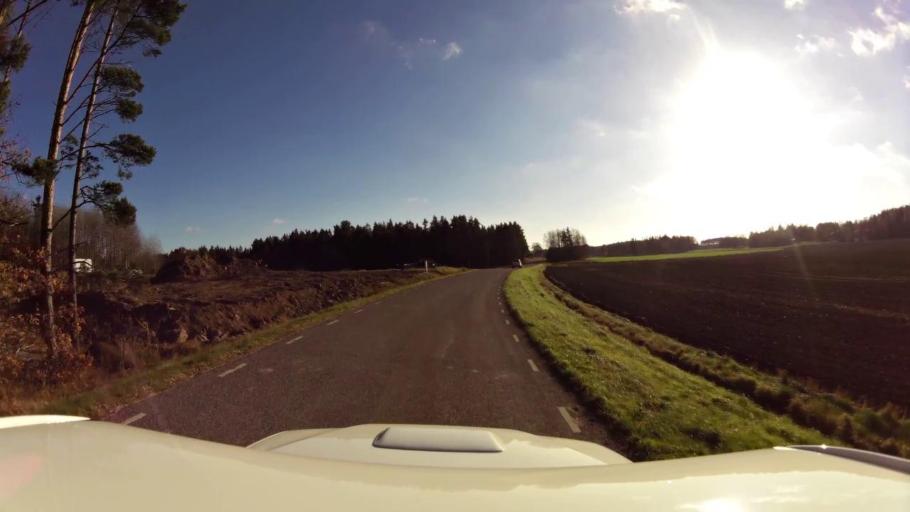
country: SE
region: OEstergoetland
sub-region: Linkopings Kommun
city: Linghem
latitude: 58.4688
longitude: 15.7663
